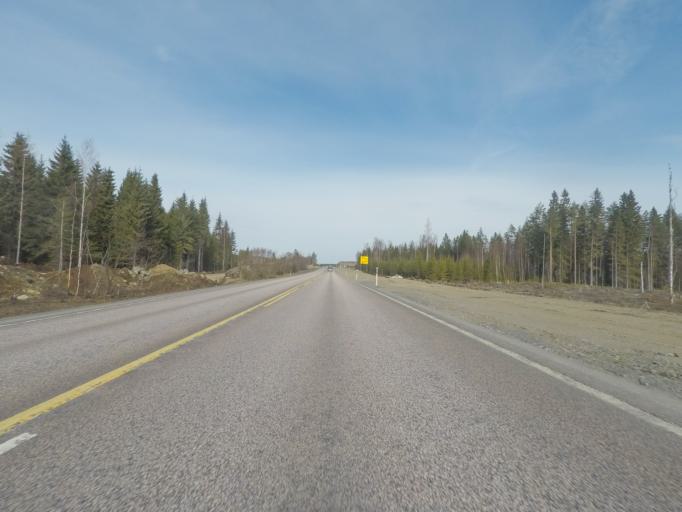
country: FI
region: Central Finland
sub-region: Joutsa
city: Leivonmaeki
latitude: 61.8534
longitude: 26.1020
